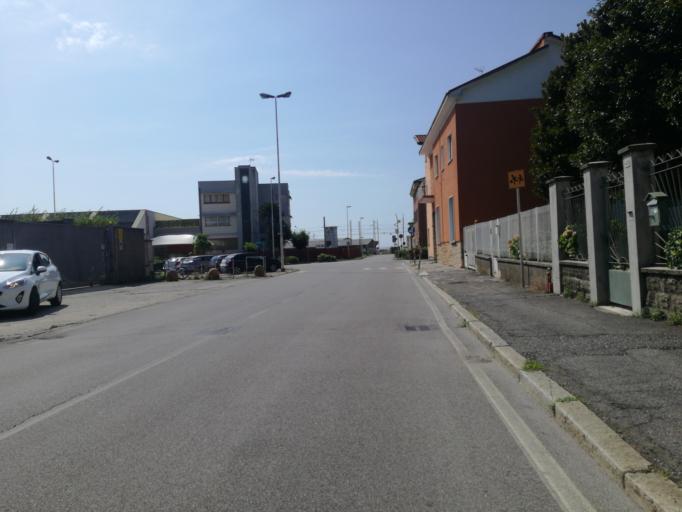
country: IT
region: Lombardy
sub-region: Provincia di Bergamo
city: Calusco d'Adda
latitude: 45.6853
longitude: 9.4730
